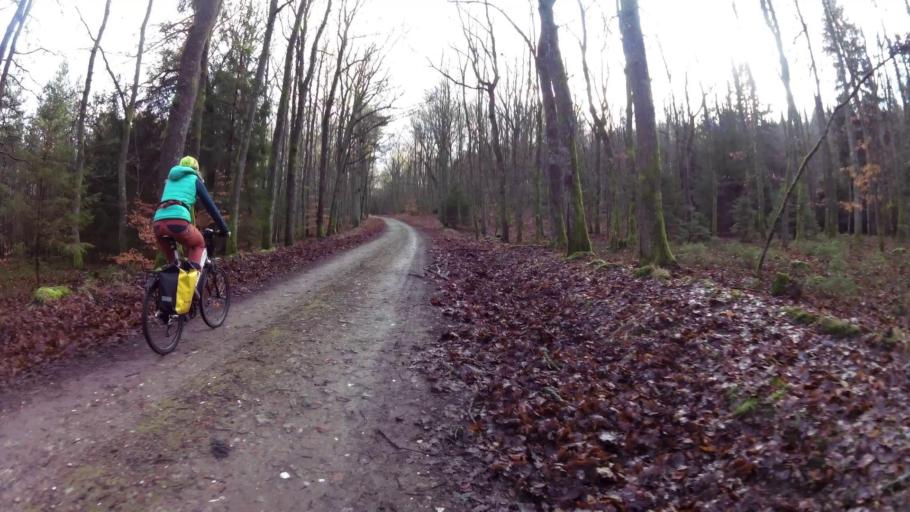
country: PL
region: West Pomeranian Voivodeship
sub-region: Powiat koszalinski
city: Sianow
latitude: 54.1144
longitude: 16.2966
